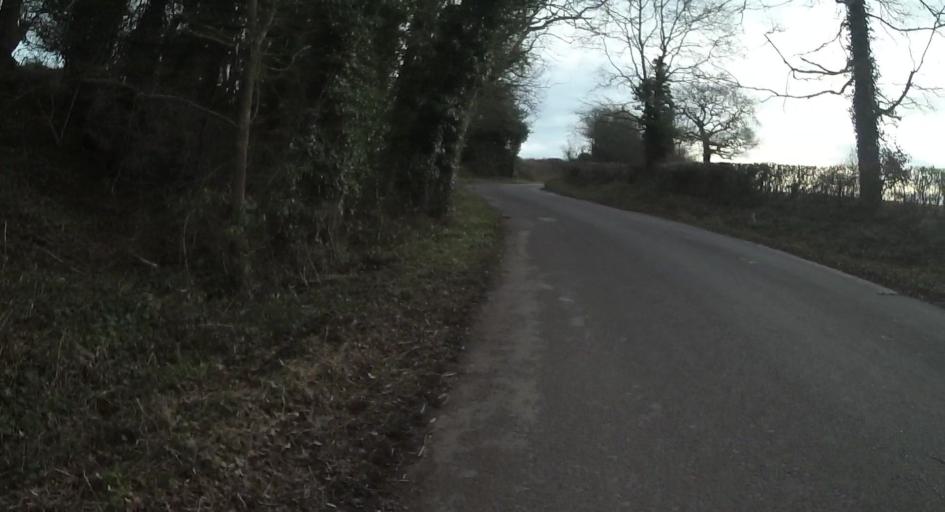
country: GB
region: England
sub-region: West Berkshire
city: Theale
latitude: 51.4127
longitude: -1.0680
